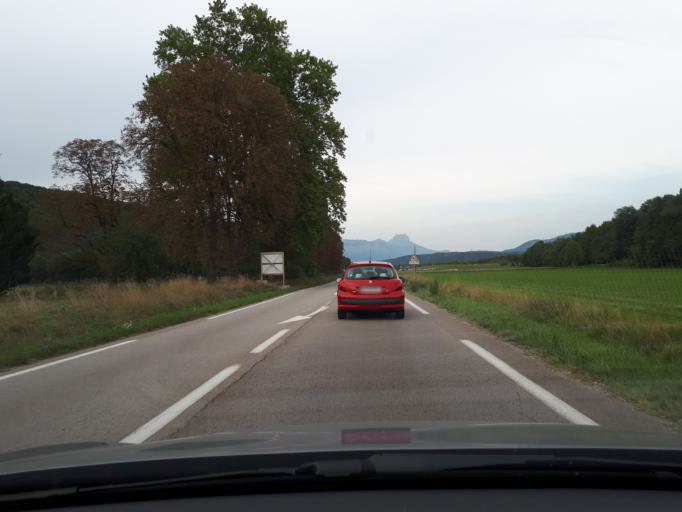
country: FR
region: Rhone-Alpes
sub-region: Departement de l'Isere
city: Vif
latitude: 45.0689
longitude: 5.6741
